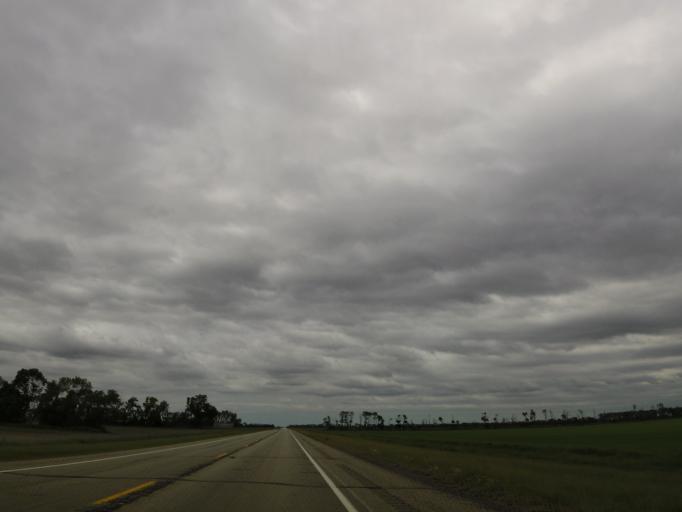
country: US
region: North Dakota
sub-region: Walsh County
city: Grafton
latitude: 48.5174
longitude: -97.4477
